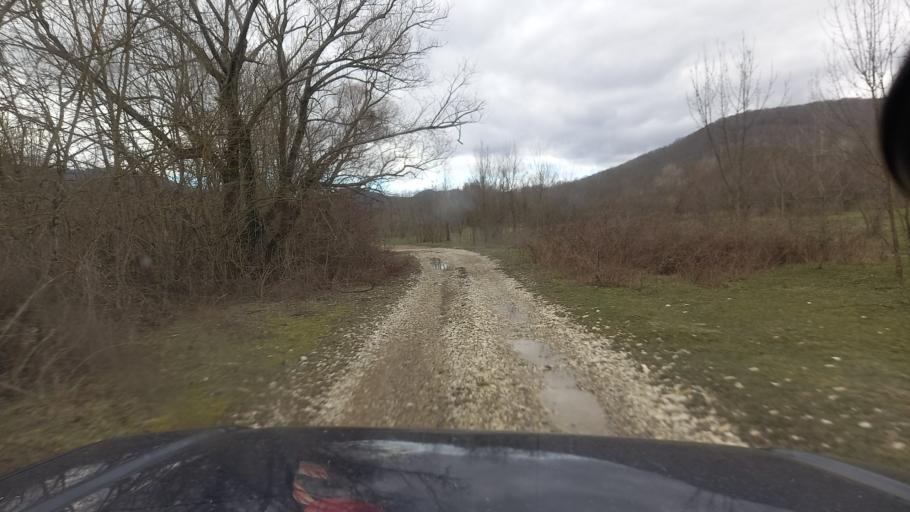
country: RU
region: Krasnodarskiy
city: Pshada
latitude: 44.4869
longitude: 38.4079
